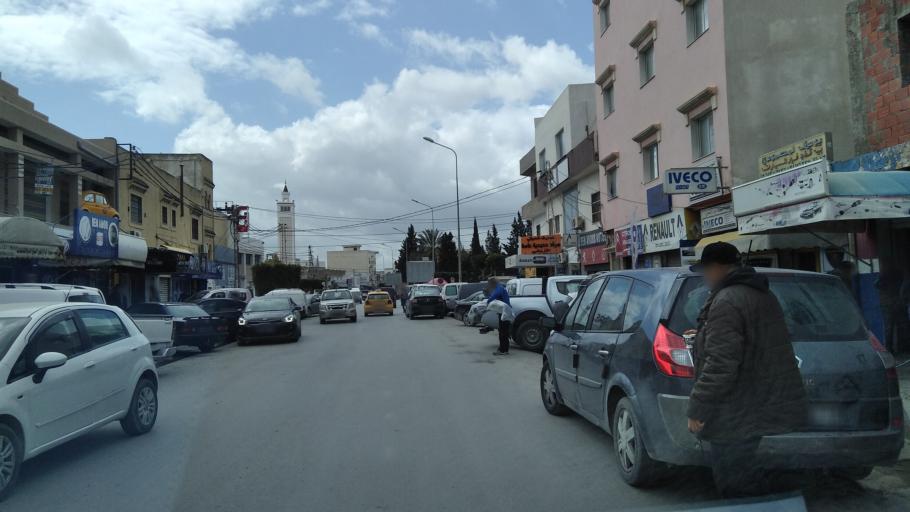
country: TN
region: Bin 'Arus
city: Ben Arous
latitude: 36.7593
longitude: 10.2230
